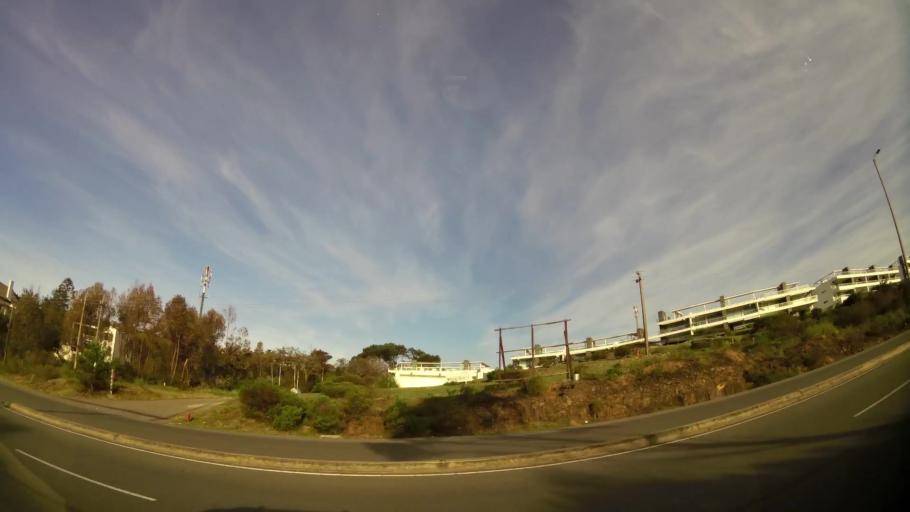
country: UY
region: Maldonado
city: Maldonado
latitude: -34.8894
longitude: -55.0382
